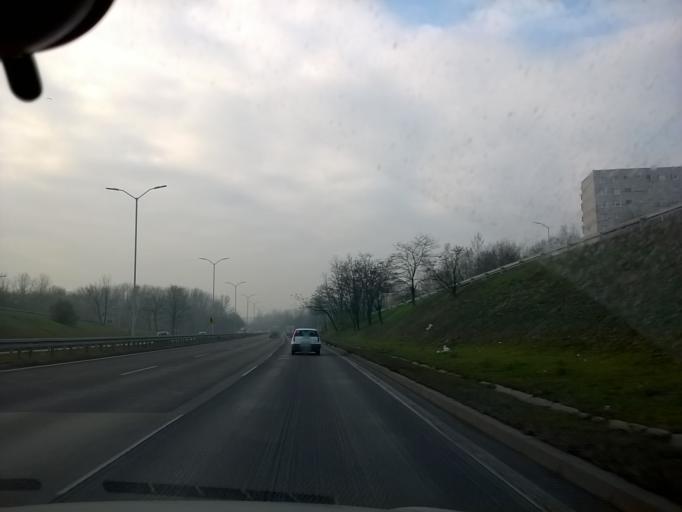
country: PL
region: Silesian Voivodeship
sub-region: Swietochlowice
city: Swietochlowice
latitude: 50.2966
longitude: 18.9164
